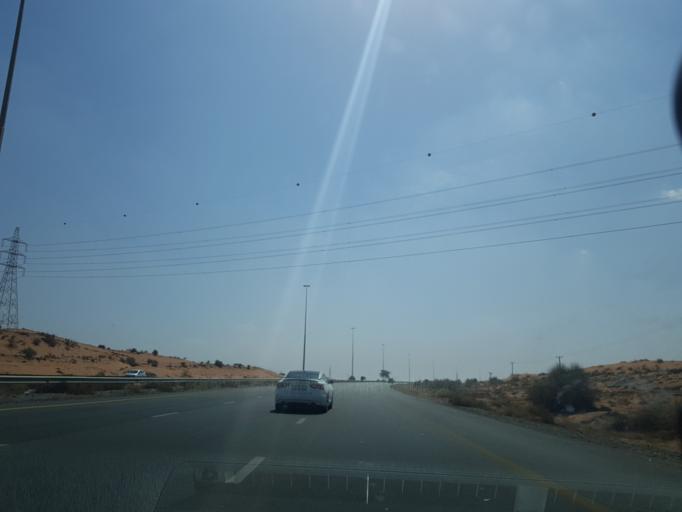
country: AE
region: Ra's al Khaymah
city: Ras al-Khaimah
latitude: 25.6857
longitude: 55.8821
